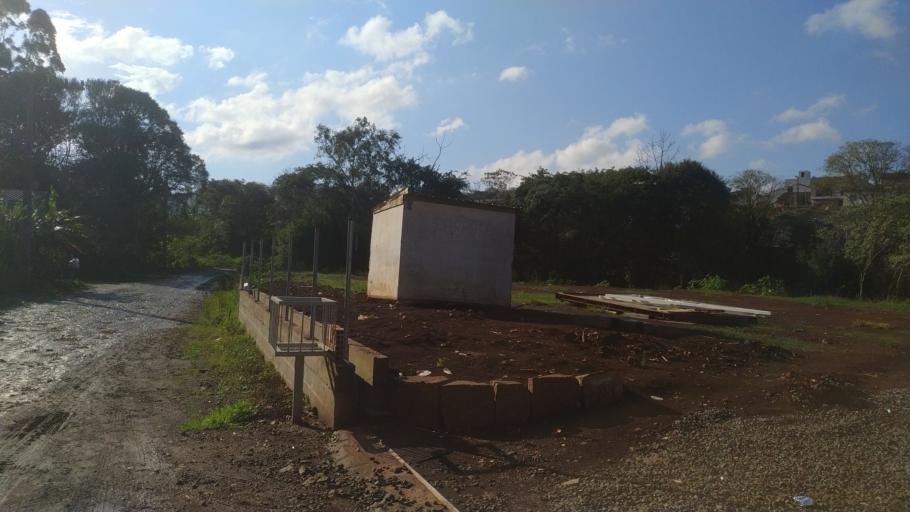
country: BR
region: Santa Catarina
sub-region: Chapeco
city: Chapeco
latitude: -27.0644
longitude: -52.6077
